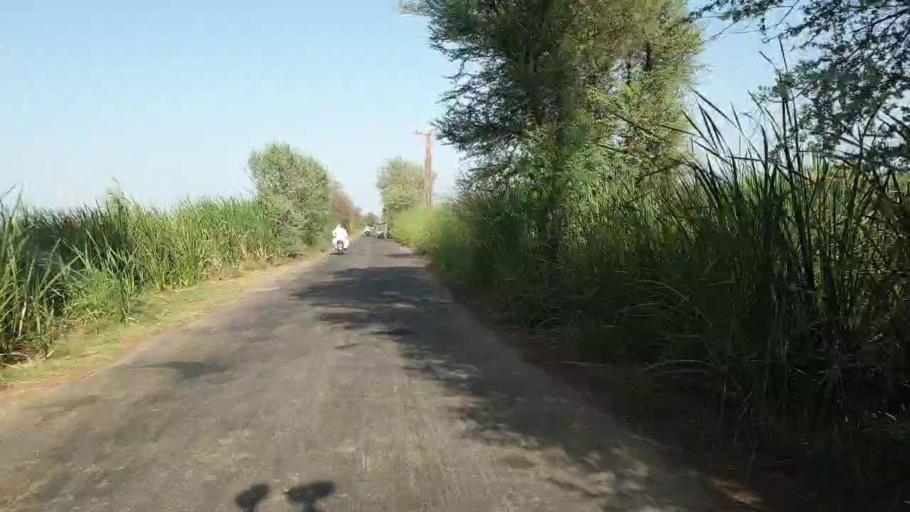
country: PK
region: Sindh
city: Nawabshah
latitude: 26.3756
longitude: 68.4641
